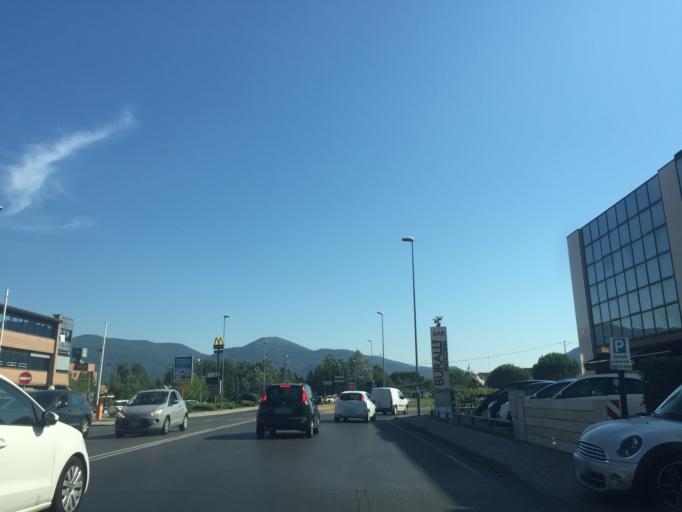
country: IT
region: Tuscany
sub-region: Provincia di Lucca
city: Lucca
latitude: 43.8329
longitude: 10.4942
